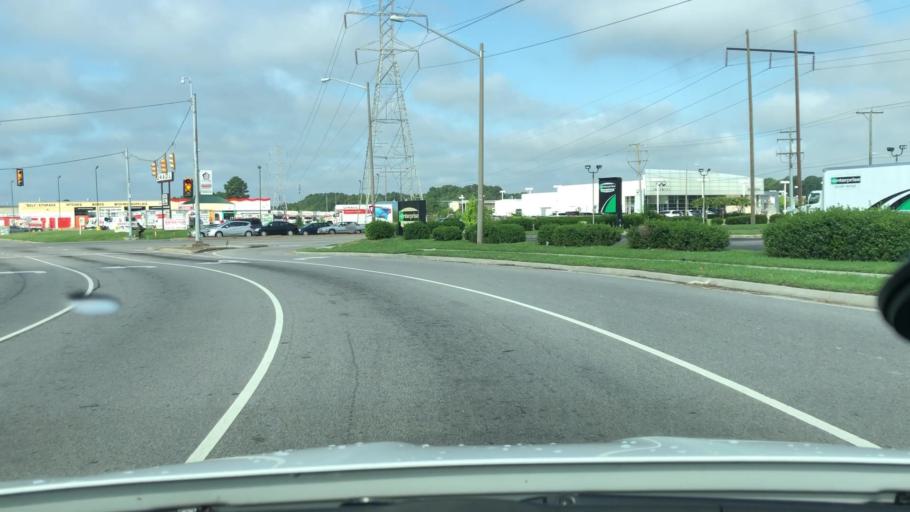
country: US
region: Virginia
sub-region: City of Chesapeake
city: Chesapeake
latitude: 36.7905
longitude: -76.2370
